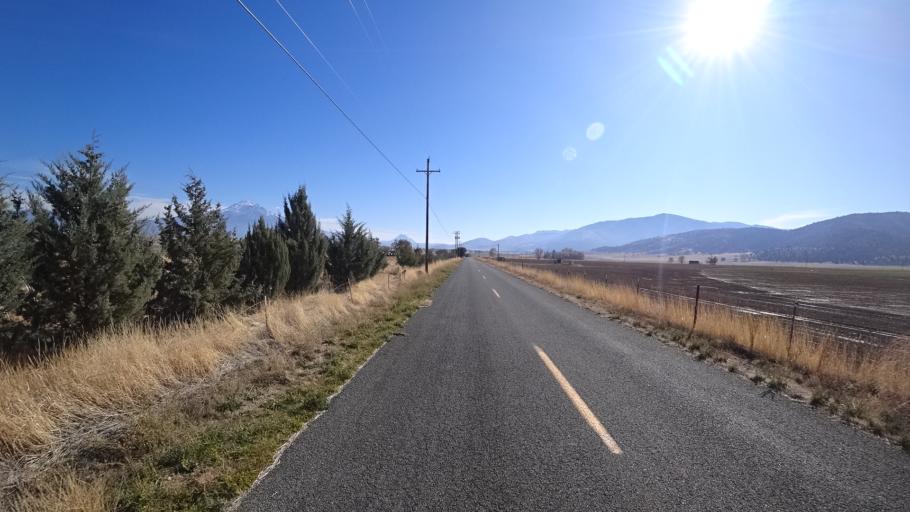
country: US
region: California
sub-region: Siskiyou County
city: Montague
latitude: 41.5421
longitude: -122.5381
